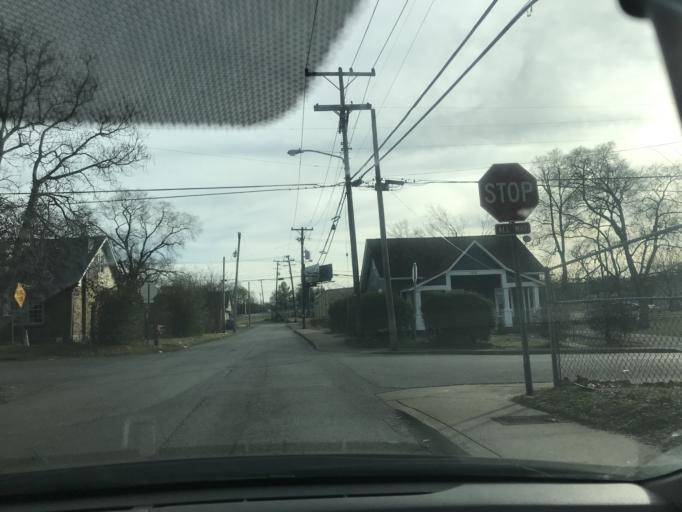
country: US
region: Tennessee
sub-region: Davidson County
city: Nashville
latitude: 36.1694
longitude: -86.8170
